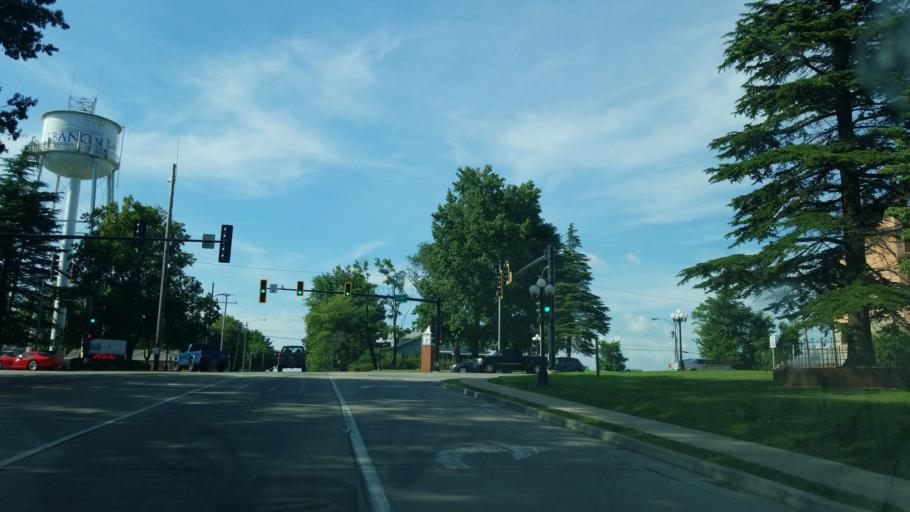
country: US
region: Illinois
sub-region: Saint Clair County
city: Lebanon
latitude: 38.6035
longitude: -89.8076
